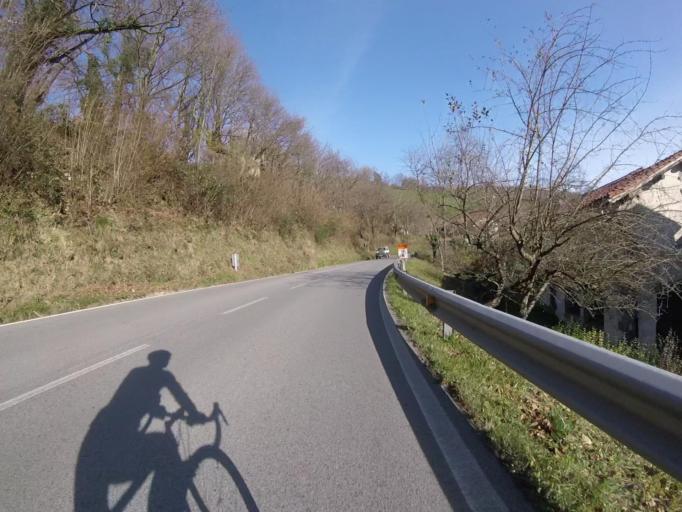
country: ES
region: Navarre
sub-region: Provincia de Navarra
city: Leitza
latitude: 43.0856
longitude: -1.9088
